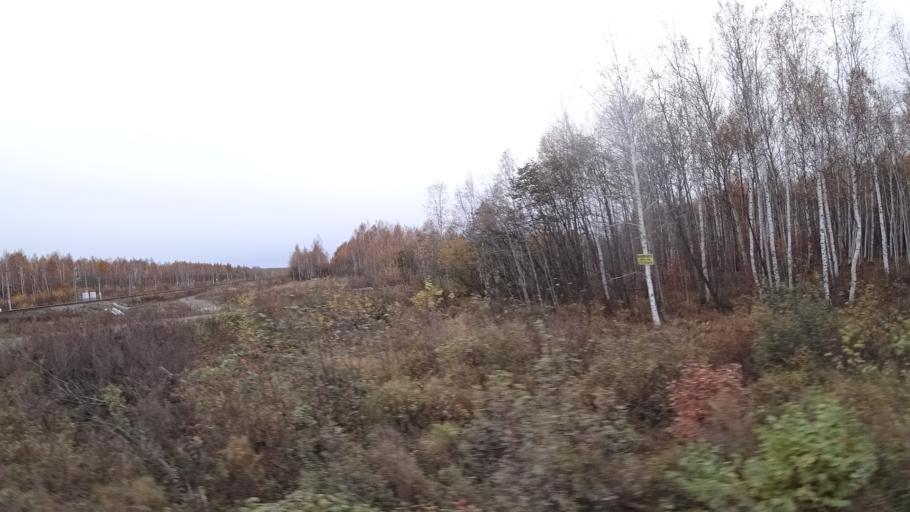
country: RU
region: Khabarovsk Krai
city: Amursk
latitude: 49.9841
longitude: 136.3131
